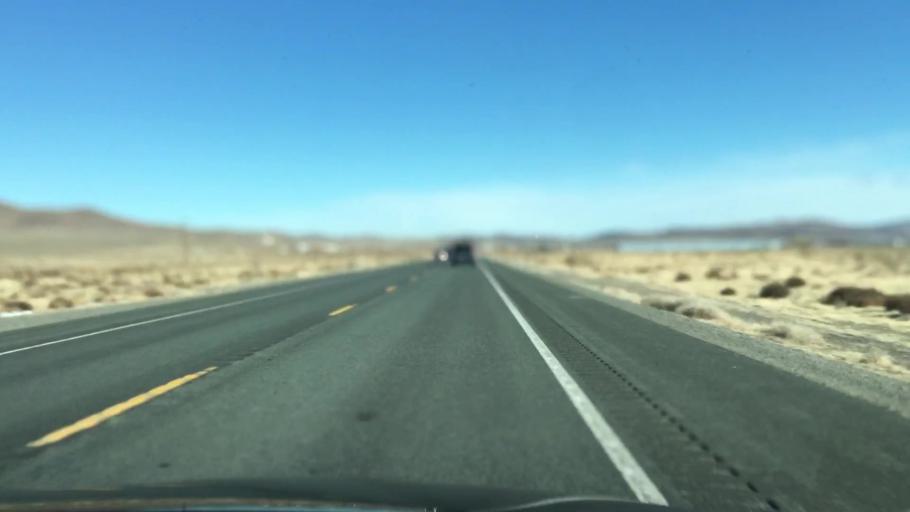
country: US
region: Nevada
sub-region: Lyon County
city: Silver Springs
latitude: 39.4050
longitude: -119.2552
